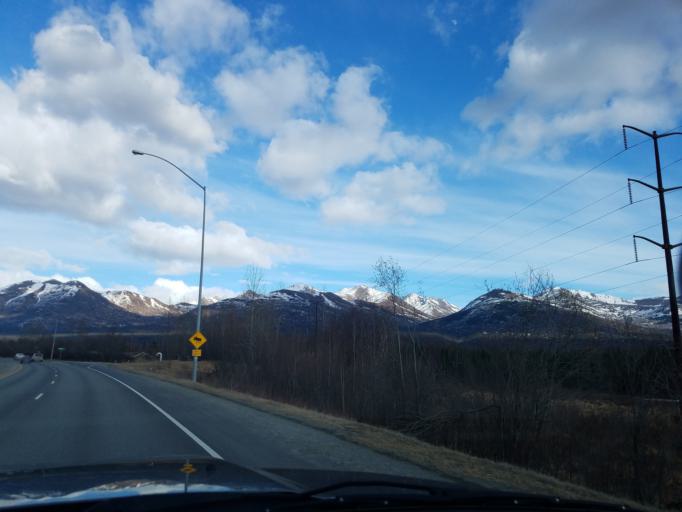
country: US
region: Alaska
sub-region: Anchorage Municipality
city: Elmendorf Air Force Base
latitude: 61.1807
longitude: -149.7440
